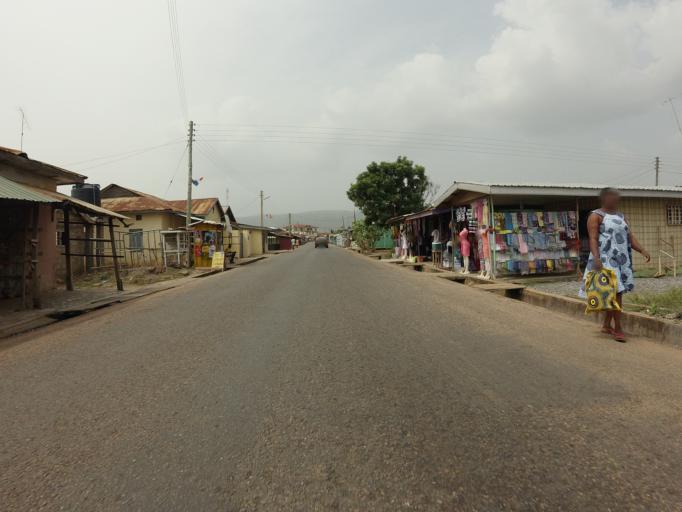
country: GH
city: Akropong
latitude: 6.1040
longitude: -0.0116
